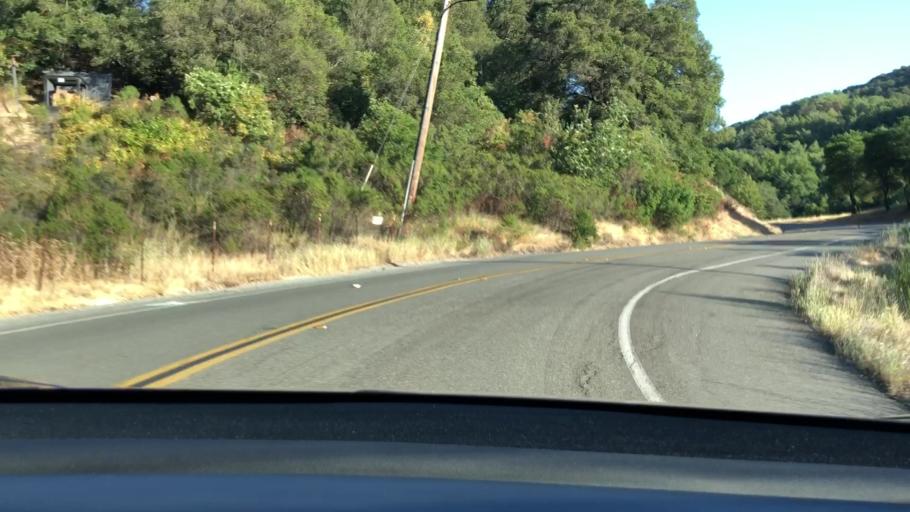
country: US
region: California
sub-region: Santa Clara County
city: Saratoga
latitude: 37.2777
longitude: -122.0703
